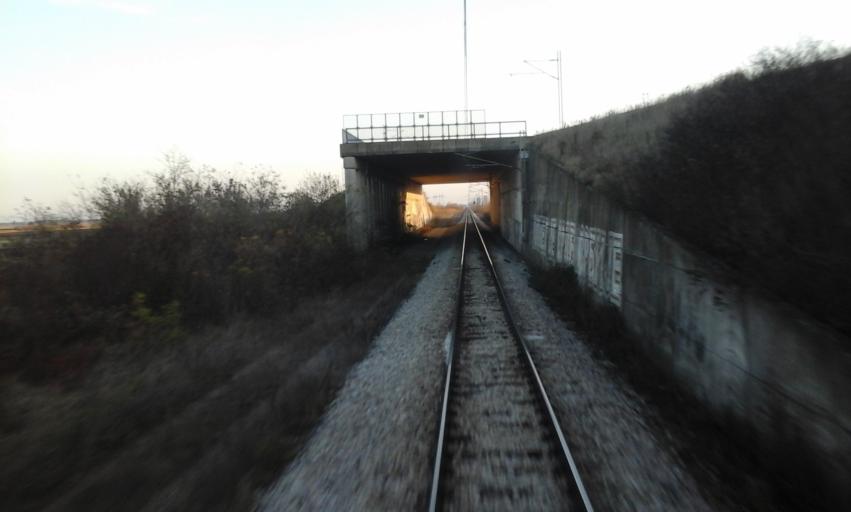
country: RS
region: Autonomna Pokrajina Vojvodina
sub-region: Sremski Okrug
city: Ingija
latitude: 45.0165
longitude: 20.1156
